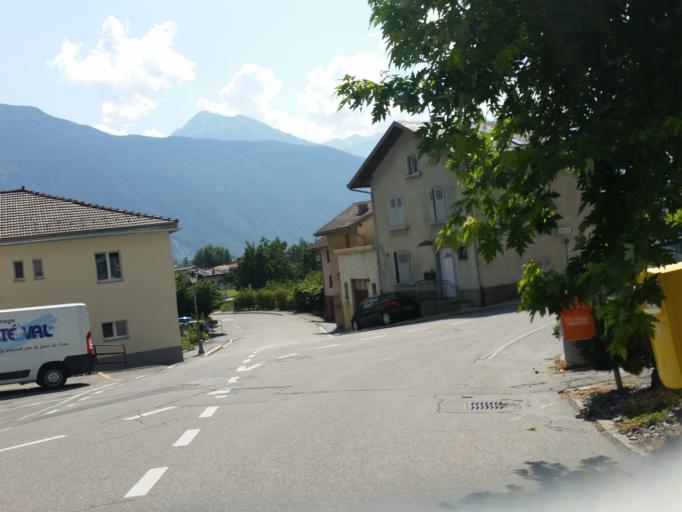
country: CH
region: Valais
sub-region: Martigny District
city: Fully
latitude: 46.1450
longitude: 7.1251
